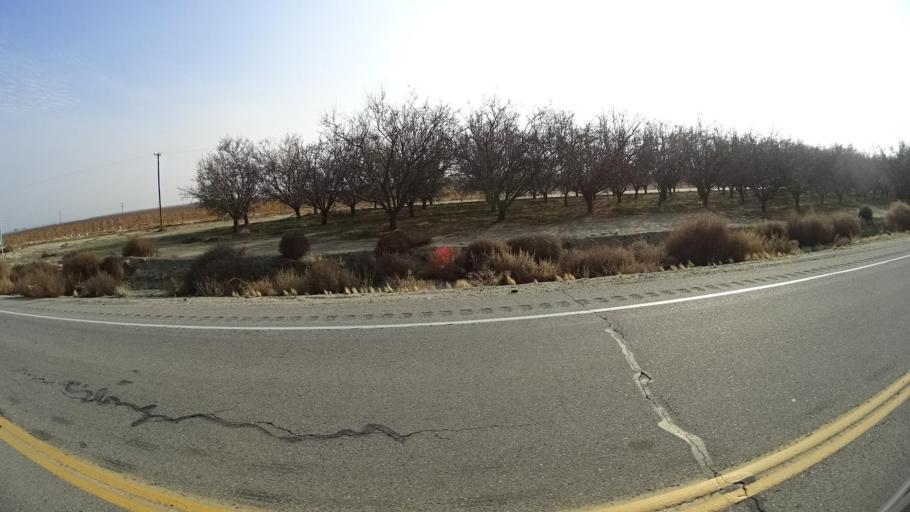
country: US
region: California
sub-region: Kern County
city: Arvin
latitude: 35.0441
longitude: -118.9181
